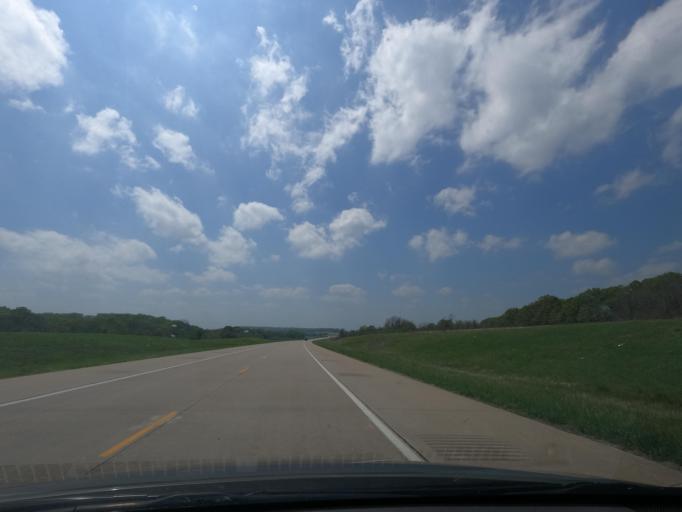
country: US
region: Kansas
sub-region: Wilson County
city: Fredonia
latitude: 37.6137
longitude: -95.9325
